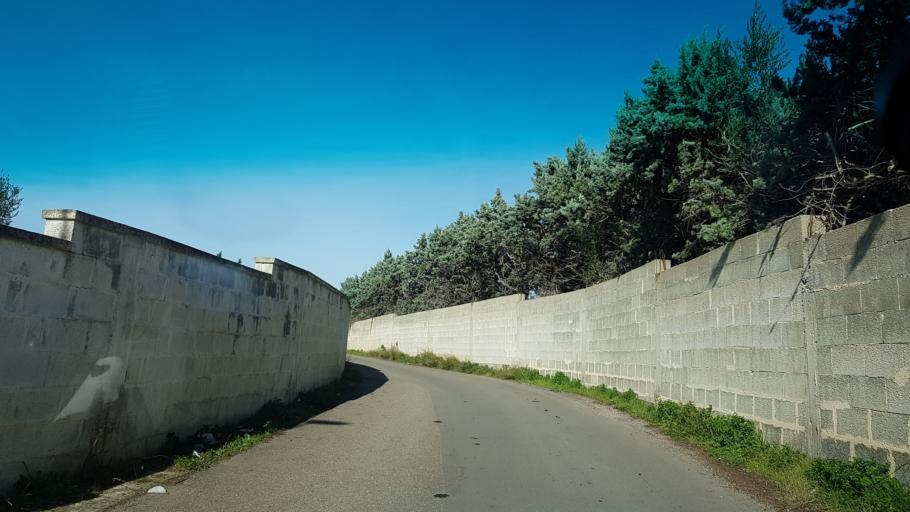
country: IT
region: Apulia
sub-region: Provincia di Lecce
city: Arnesano
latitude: 40.3591
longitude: 18.1060
